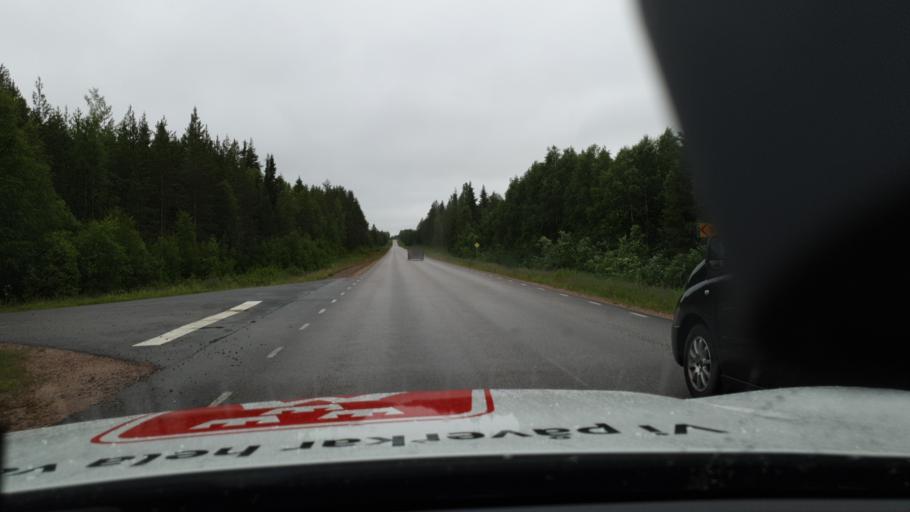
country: SE
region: Norrbotten
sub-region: Overtornea Kommun
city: OEvertornea
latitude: 66.5170
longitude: 23.7453
